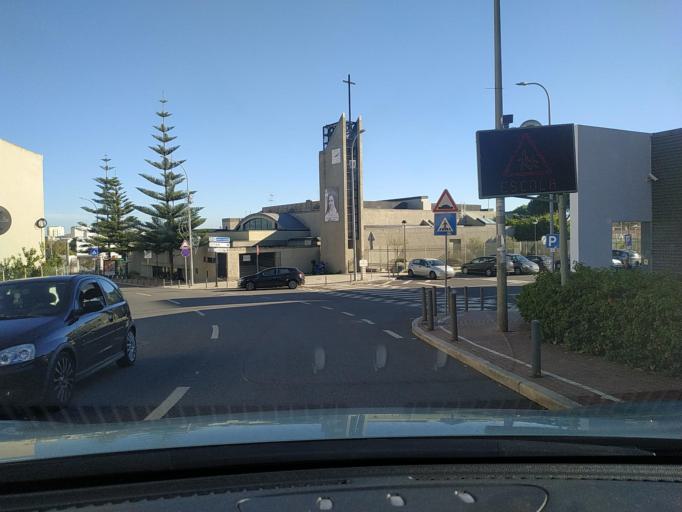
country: PT
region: Lisbon
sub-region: Odivelas
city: Pontinha
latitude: 38.7668
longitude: -9.2161
